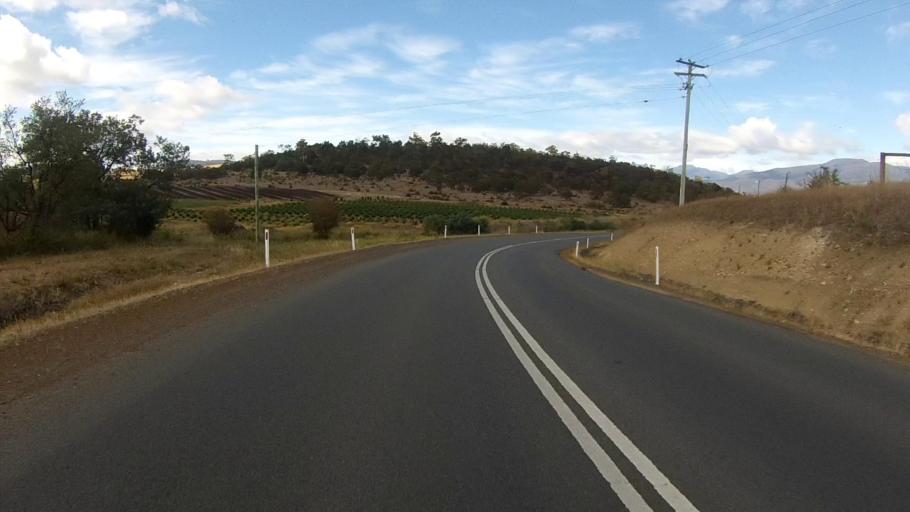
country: AU
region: Tasmania
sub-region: Brighton
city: Old Beach
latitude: -42.7403
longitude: 147.2881
